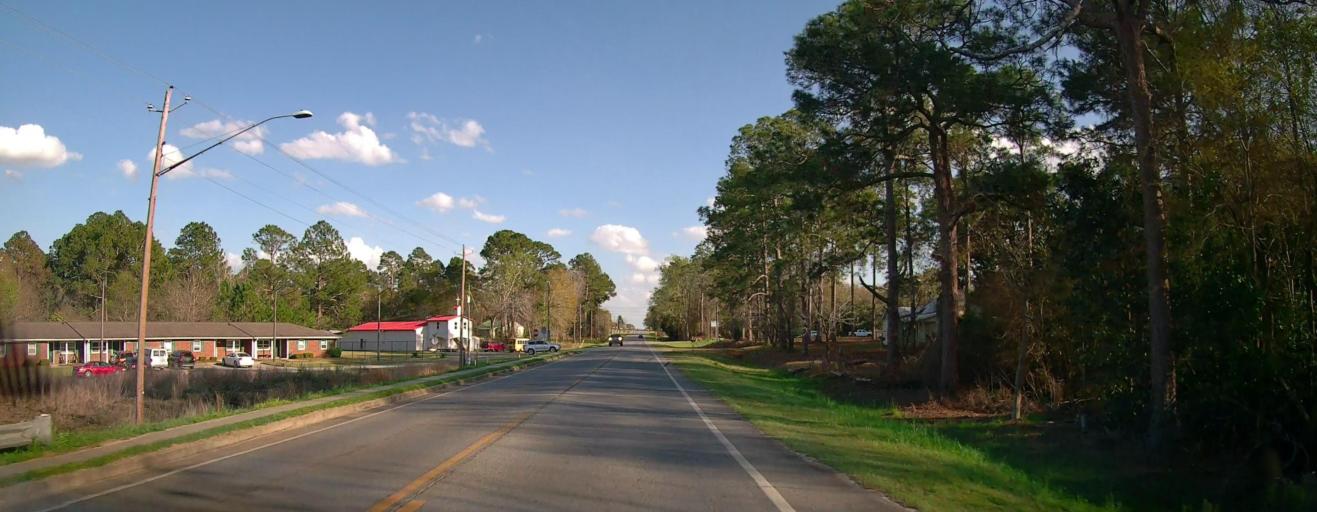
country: US
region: Georgia
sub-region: Toombs County
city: Lyons
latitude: 32.2001
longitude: -82.3157
